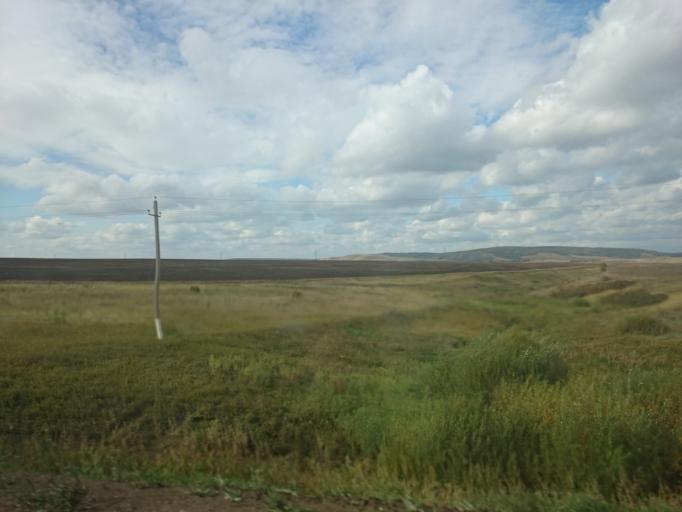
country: RU
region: Samara
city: Kamyshla
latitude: 54.0706
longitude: 52.1848
